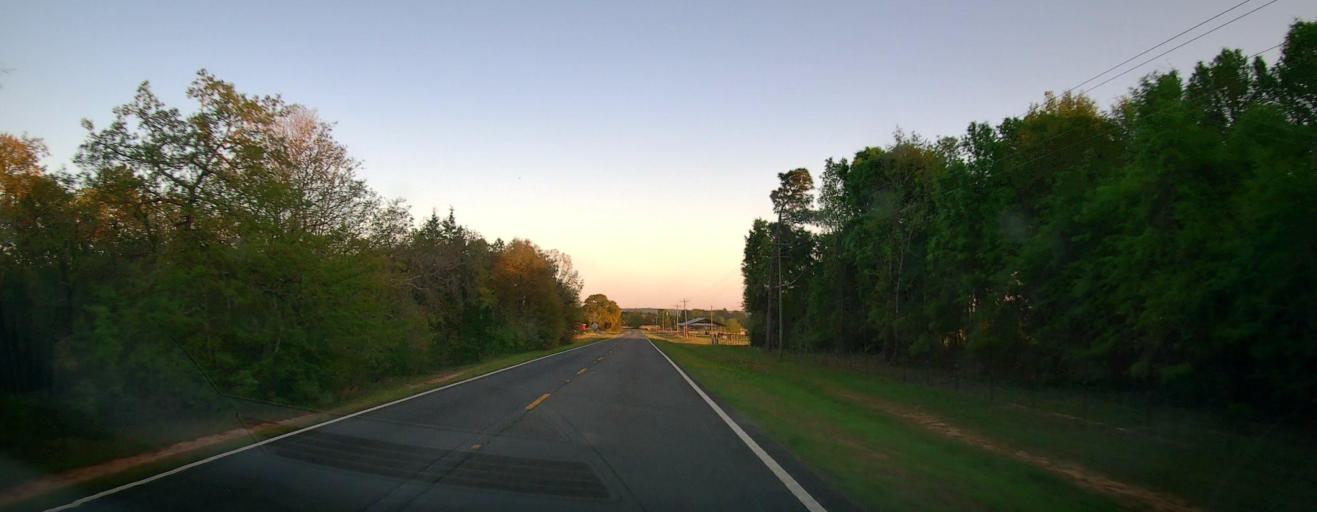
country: US
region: Georgia
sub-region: Marion County
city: Buena Vista
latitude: 32.4633
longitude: -84.6323
